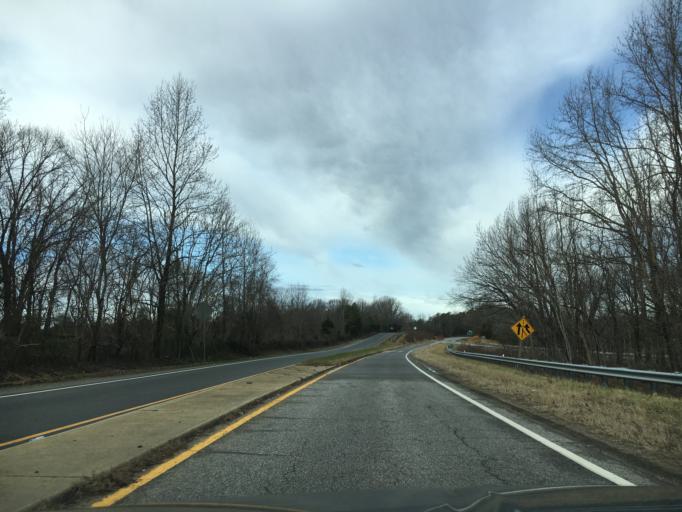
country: US
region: Virginia
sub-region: Nottoway County
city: Crewe
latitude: 37.1909
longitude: -78.2180
